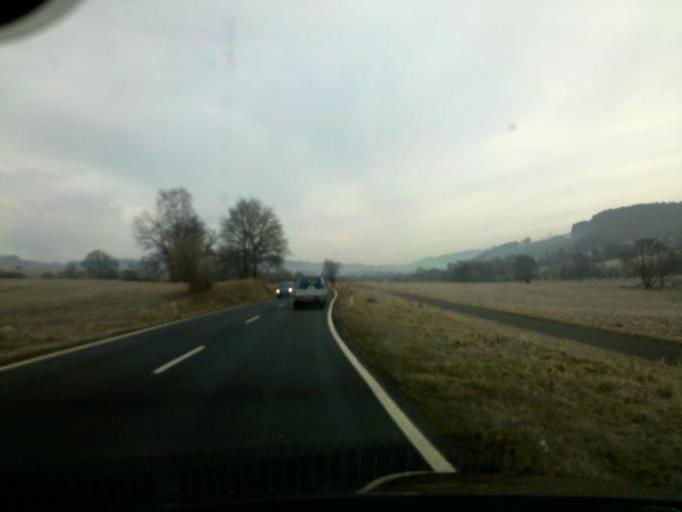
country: DE
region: Hesse
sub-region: Regierungsbezirk Giessen
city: Haiger
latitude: 50.7842
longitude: 8.2184
